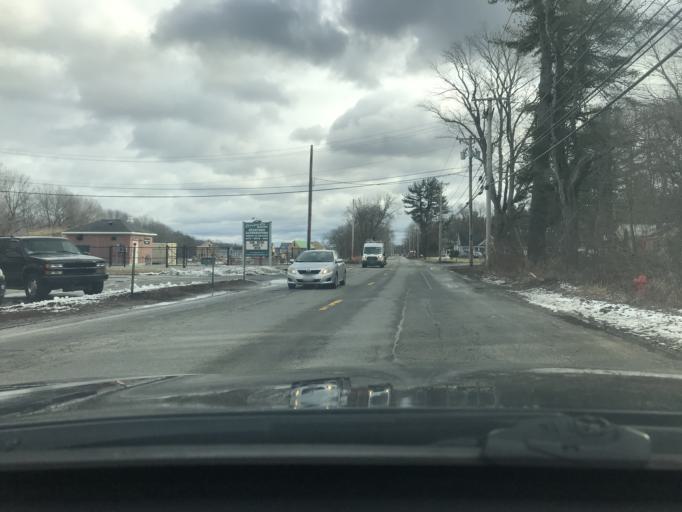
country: US
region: Massachusetts
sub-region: Middlesex County
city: Tyngsboro
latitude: 42.6682
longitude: -71.4143
